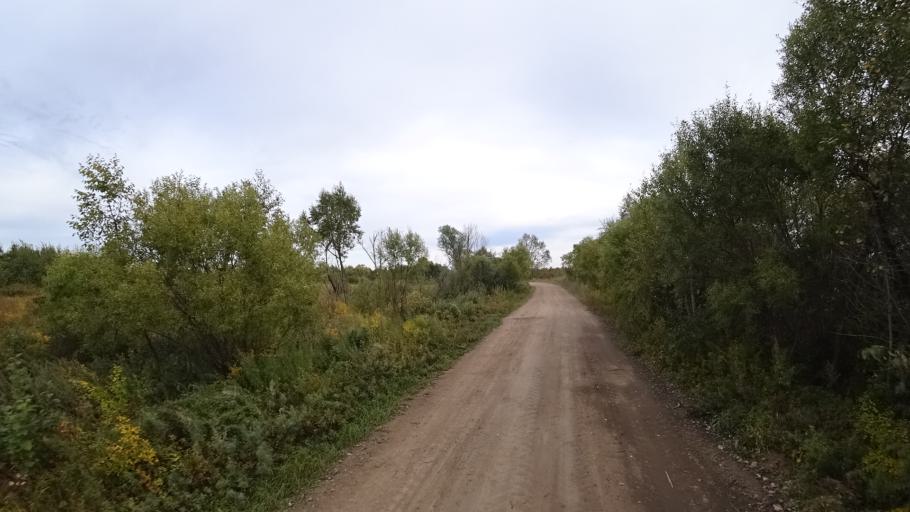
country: RU
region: Amur
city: Arkhara
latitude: 49.3412
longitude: 130.1045
